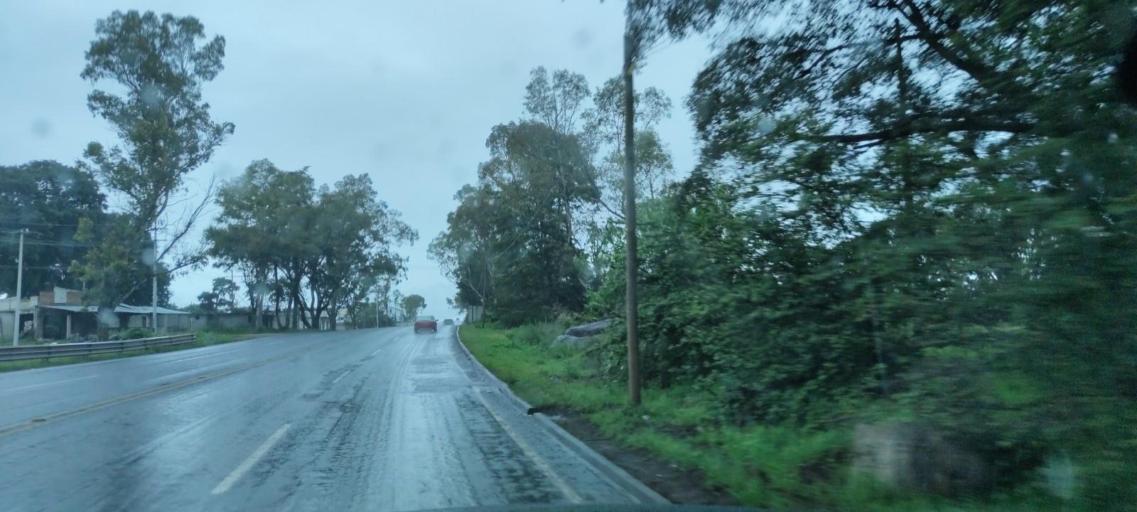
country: MX
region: Mexico
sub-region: Jilotepec
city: Doxhicho
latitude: 19.9384
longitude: -99.5658
